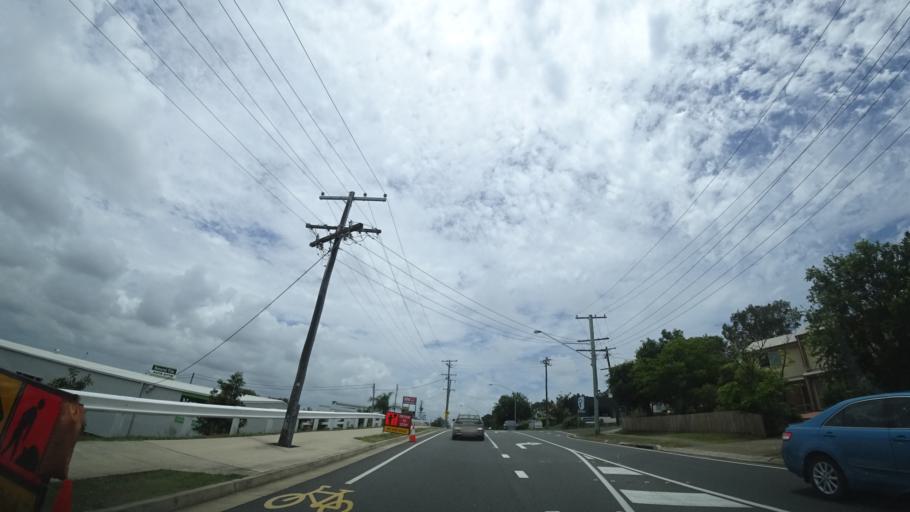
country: AU
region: Queensland
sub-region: Sunshine Coast
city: Mooloolaba
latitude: -26.6705
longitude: 153.0958
